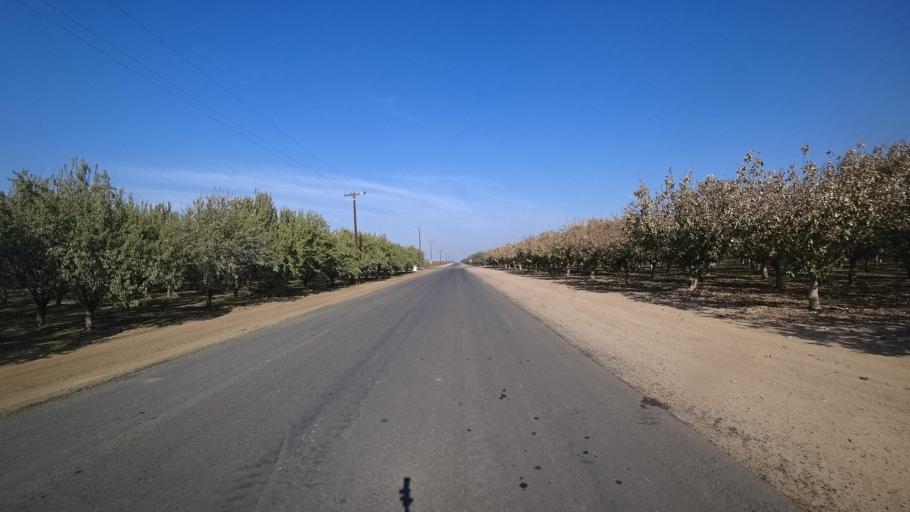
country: US
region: California
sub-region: Kern County
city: McFarland
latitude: 35.6444
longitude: -119.1867
